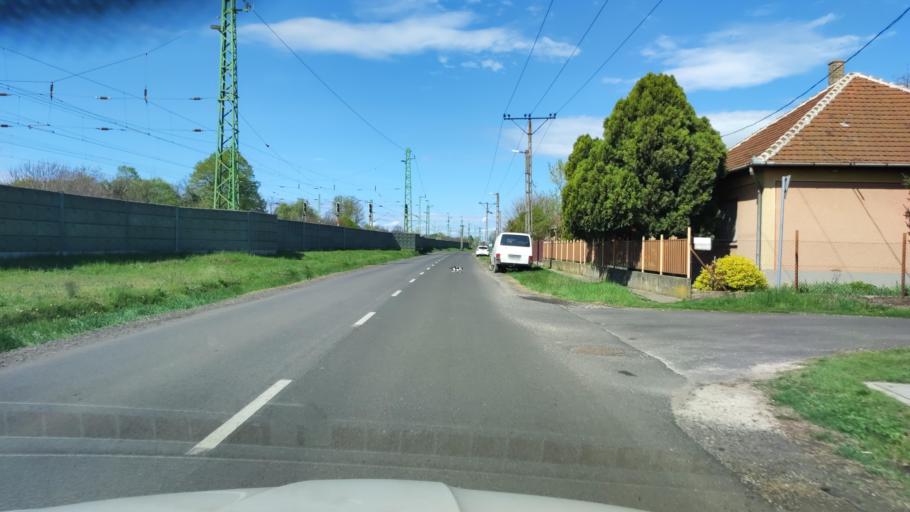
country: HU
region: Pest
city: Abony
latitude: 47.1726
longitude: 20.0094
